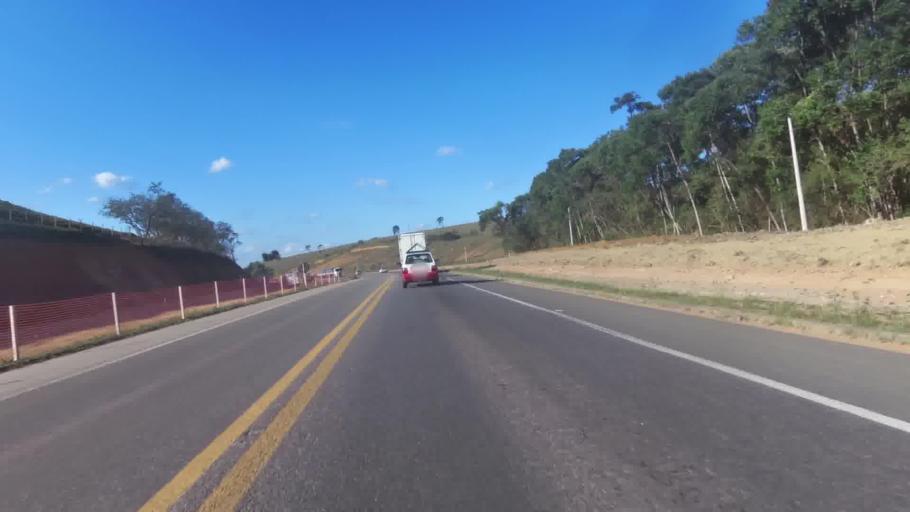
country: BR
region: Espirito Santo
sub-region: Alfredo Chaves
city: Alfredo Chaves
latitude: -20.7282
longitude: -40.7424
